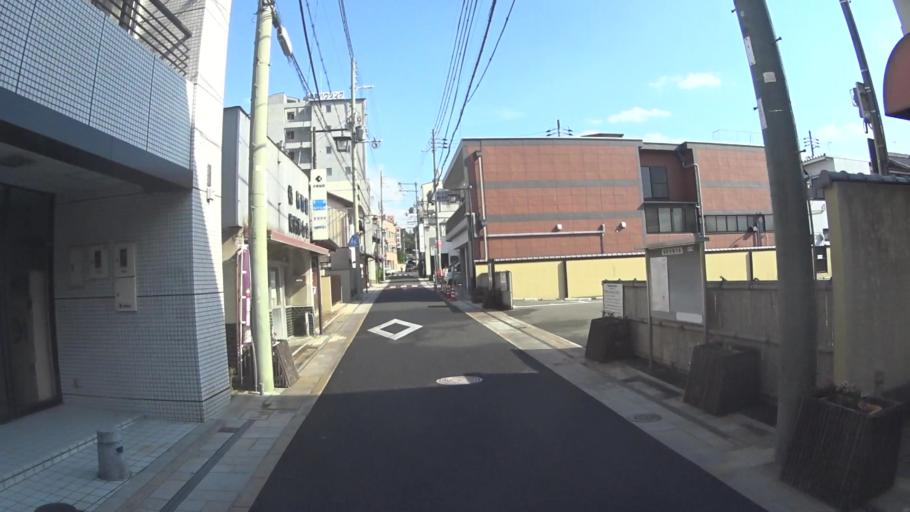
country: JP
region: Kyoto
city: Kameoka
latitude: 35.0151
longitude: 135.5771
